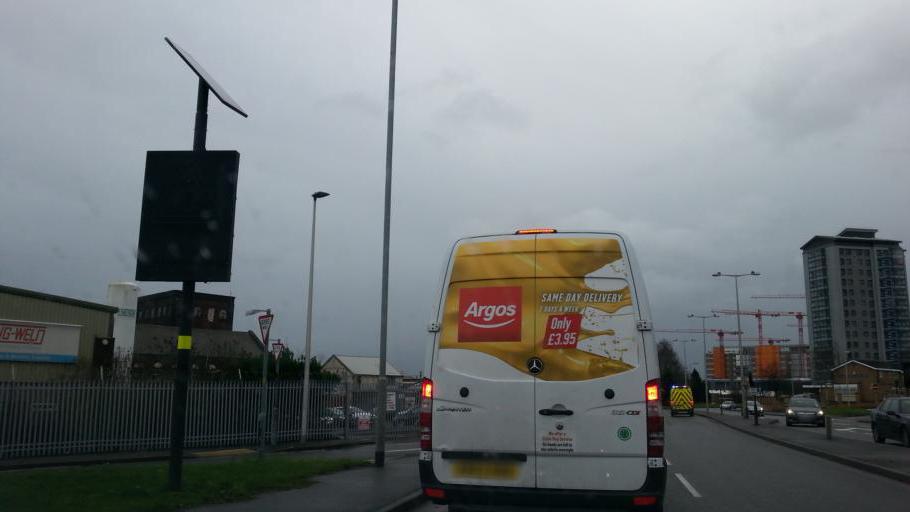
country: GB
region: England
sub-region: Sandwell
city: Smethwick
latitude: 52.4955
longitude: -1.9558
